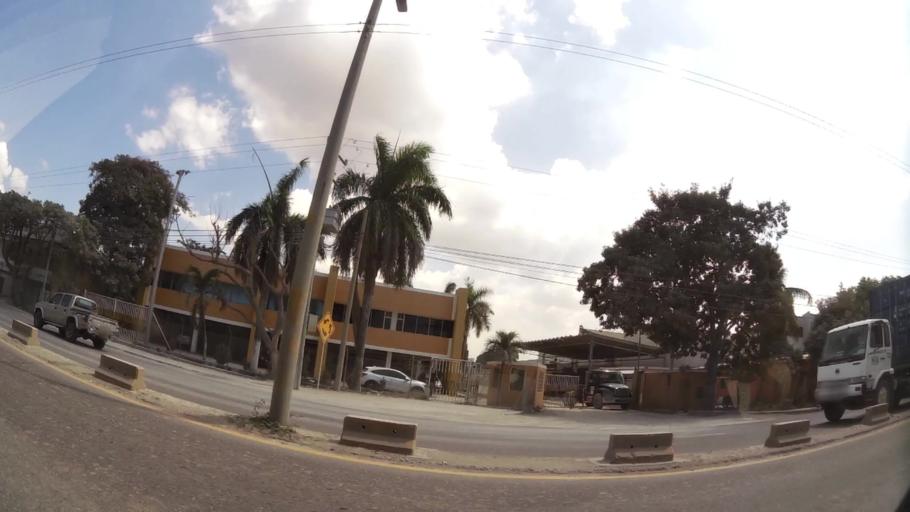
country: CO
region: Bolivar
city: Cartagena
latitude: 10.3710
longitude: -75.5060
